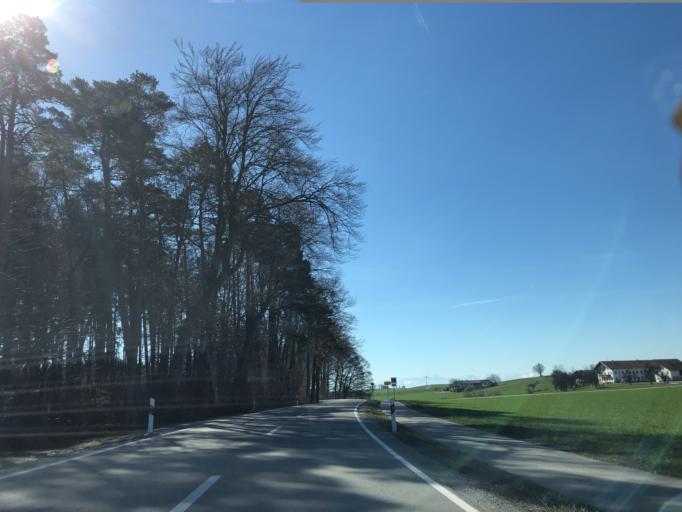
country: DE
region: Bavaria
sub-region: Upper Bavaria
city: Pfaffing
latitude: 48.0715
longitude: 12.1074
